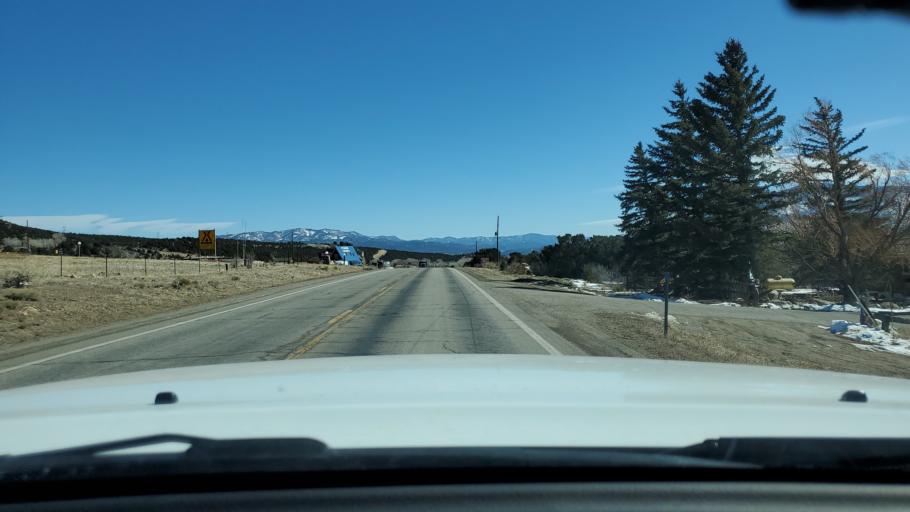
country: US
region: Colorado
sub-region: Chaffee County
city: Salida
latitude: 38.5360
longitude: -106.1769
